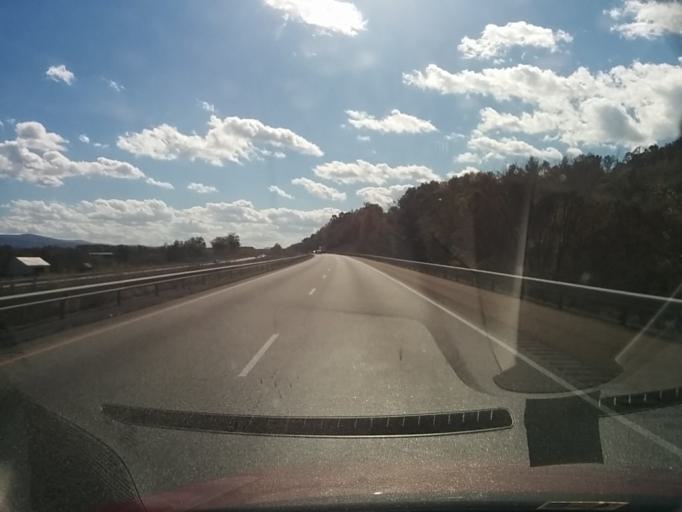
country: US
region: Virginia
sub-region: Augusta County
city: Stuarts Draft
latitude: 38.0007
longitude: -79.1743
